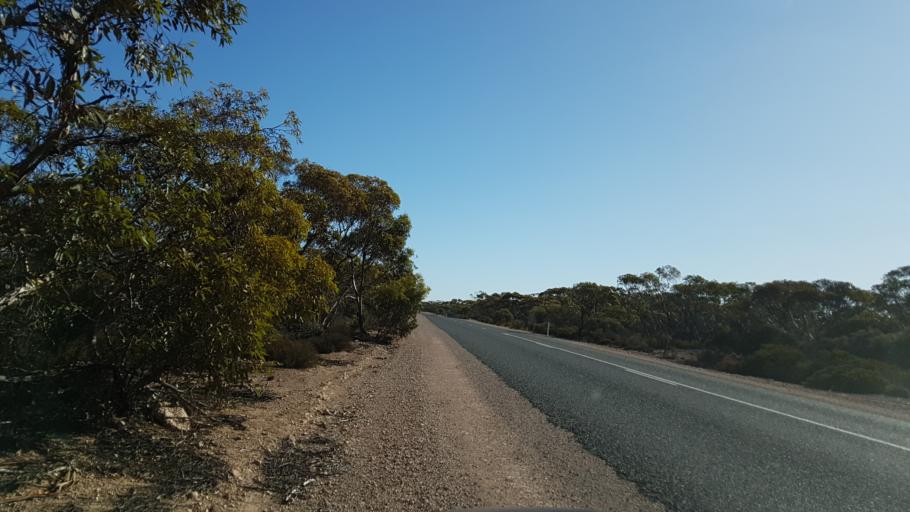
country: AU
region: South Australia
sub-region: Mid Murray
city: Mannum
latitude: -34.7934
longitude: 139.5076
